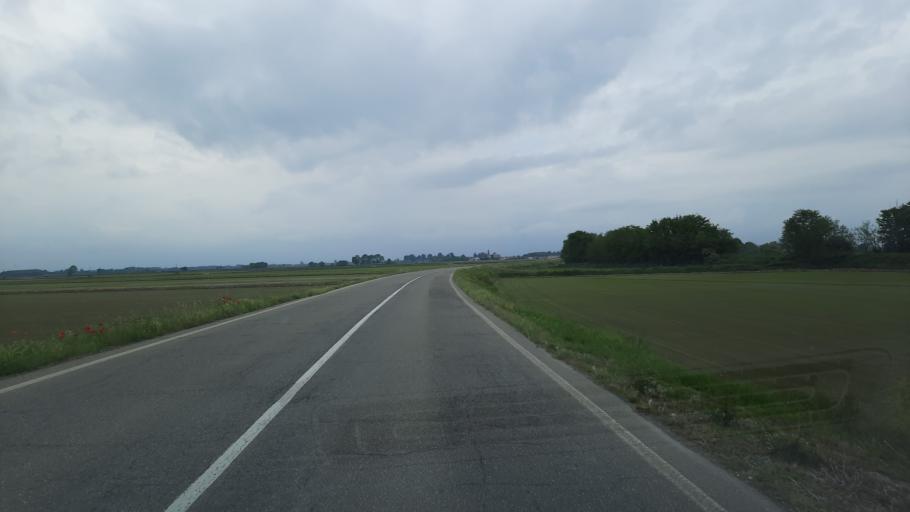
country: IT
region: Lombardy
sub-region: Provincia di Pavia
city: Langosco
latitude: 45.2010
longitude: 8.5815
